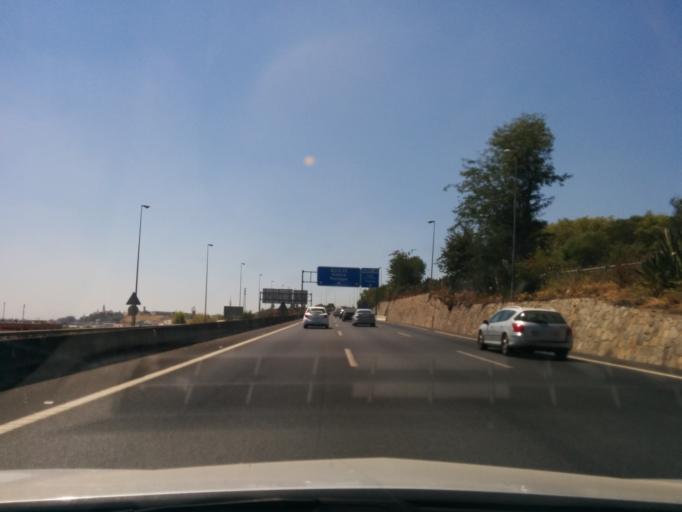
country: ES
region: Andalusia
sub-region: Provincia de Sevilla
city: Camas
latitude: 37.3869
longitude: -6.0342
